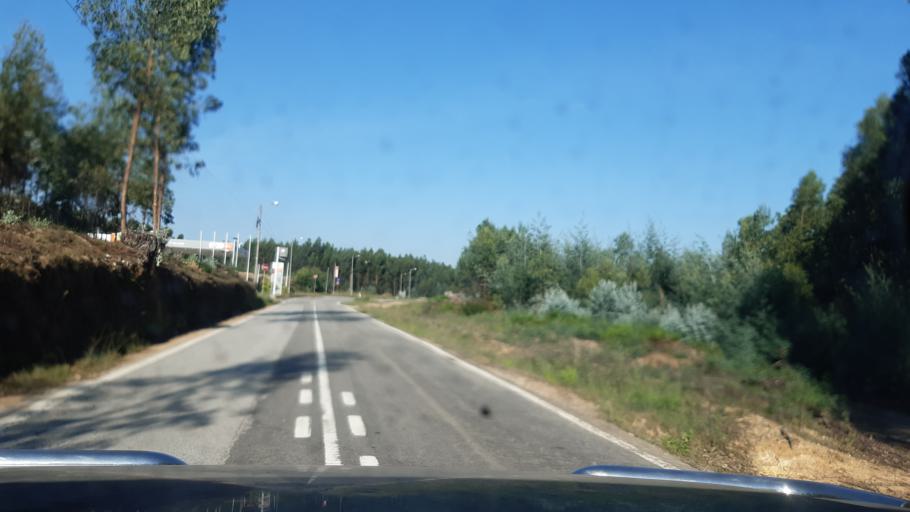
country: PT
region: Aveiro
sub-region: Agueda
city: Aguada de Cima
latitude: 40.5644
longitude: -8.3741
